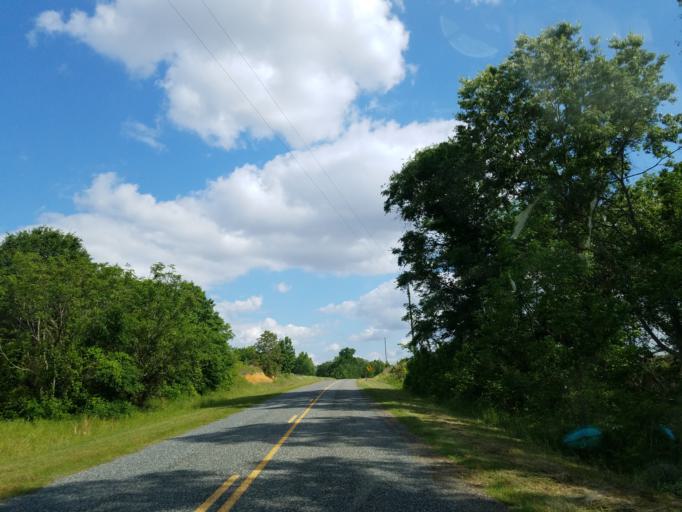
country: US
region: Georgia
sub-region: Dooly County
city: Unadilla
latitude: 32.2486
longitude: -83.7817
